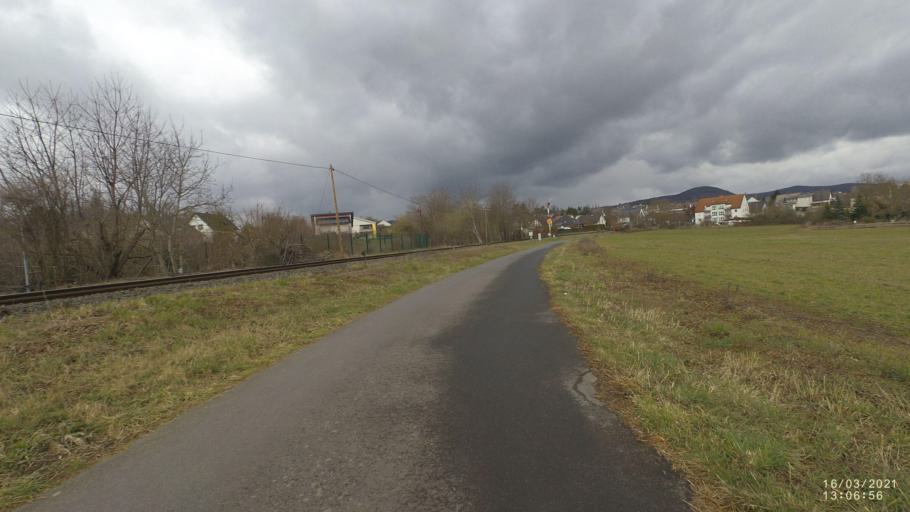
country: DE
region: Rheinland-Pfalz
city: Mendig
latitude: 50.3660
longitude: 7.2844
